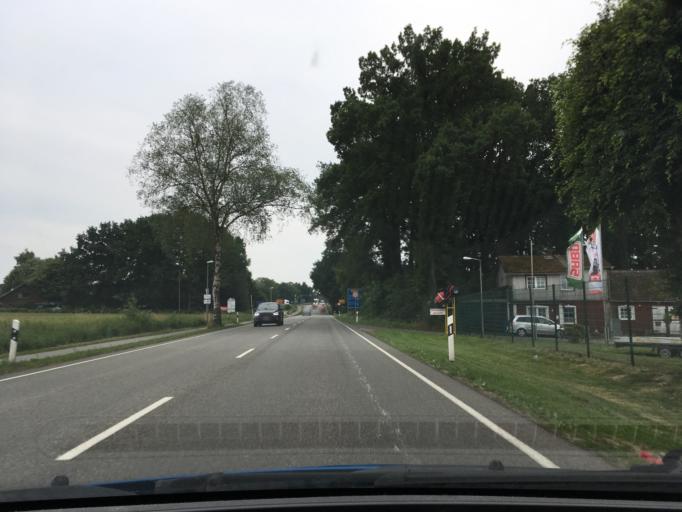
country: DE
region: Lower Saxony
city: Wenzendorf
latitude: 53.3754
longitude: 9.8038
